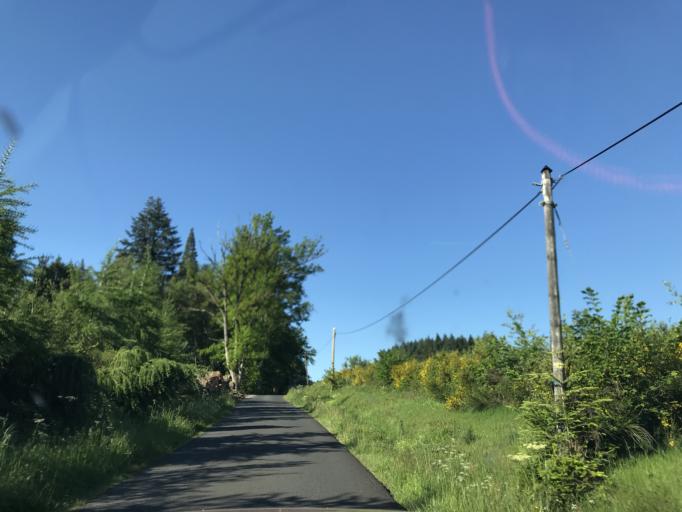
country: FR
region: Auvergne
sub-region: Departement du Puy-de-Dome
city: Job
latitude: 45.6288
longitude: 3.6794
